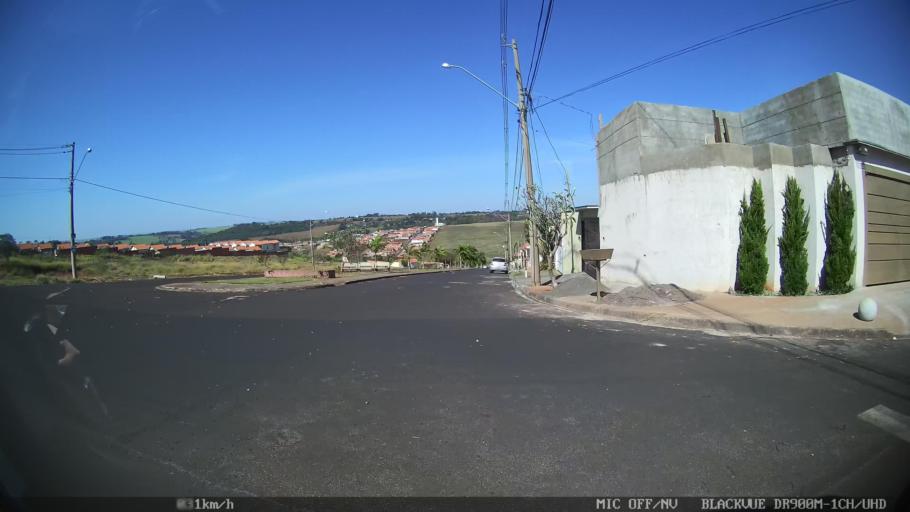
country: BR
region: Sao Paulo
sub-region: Batatais
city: Batatais
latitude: -20.8886
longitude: -47.5657
